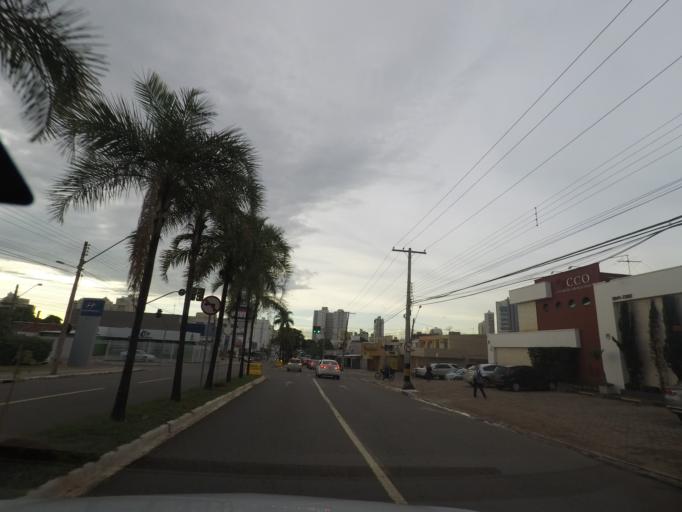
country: BR
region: Goias
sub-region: Goiania
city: Goiania
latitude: -16.6955
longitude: -49.2713
